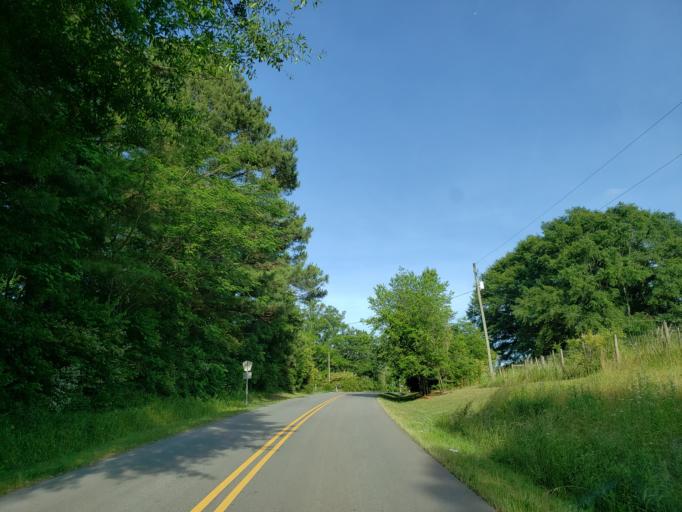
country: US
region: Georgia
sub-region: Carroll County
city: Bowdon
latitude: 33.4988
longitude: -85.3143
